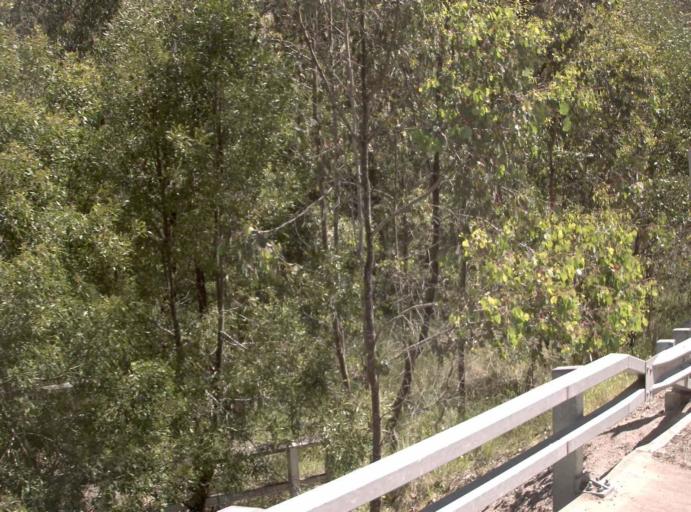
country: AU
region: Victoria
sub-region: East Gippsland
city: Lakes Entrance
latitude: -37.2322
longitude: 148.2601
